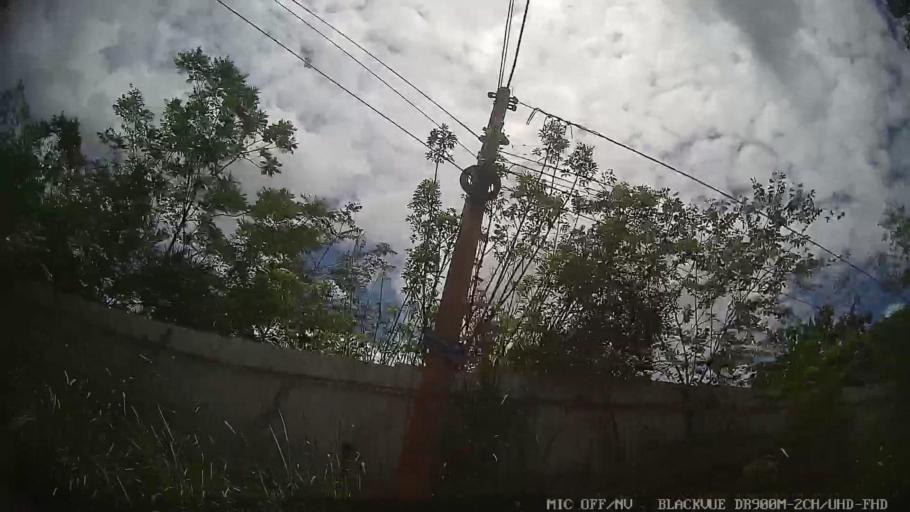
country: BR
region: Sao Paulo
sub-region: Jaguariuna
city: Jaguariuna
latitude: -22.7409
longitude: -47.0072
